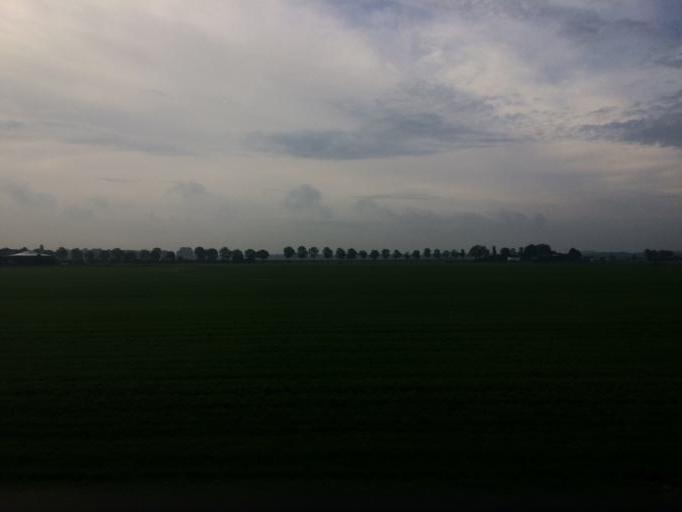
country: NL
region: North Brabant
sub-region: Gemeente Landerd
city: Schaijk
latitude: 51.7877
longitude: 5.6198
